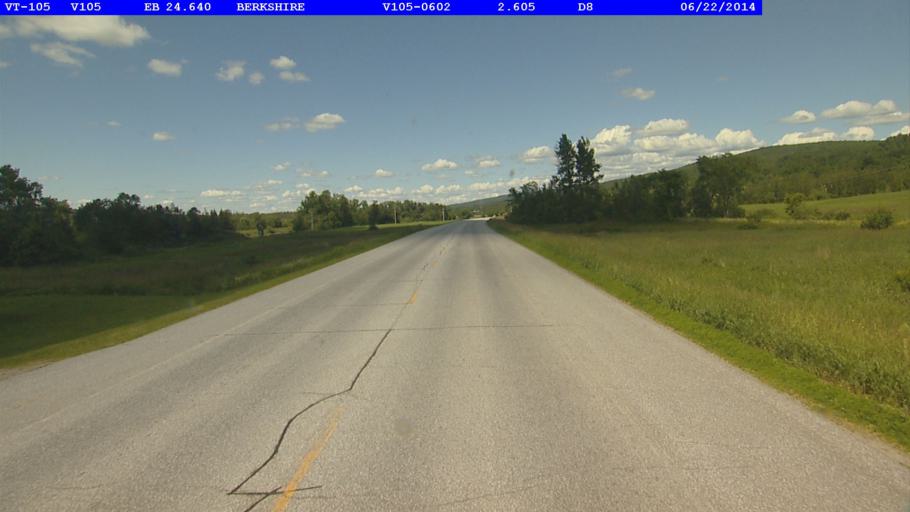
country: US
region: Vermont
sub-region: Franklin County
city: Richford
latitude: 44.9571
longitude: -72.6979
